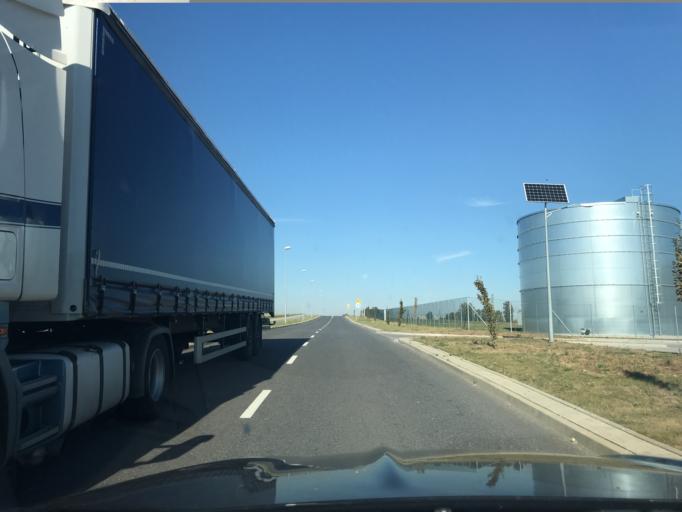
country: PL
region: Warmian-Masurian Voivodeship
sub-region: Powiat ilawski
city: Lubawa
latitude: 53.5137
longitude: 19.7257
